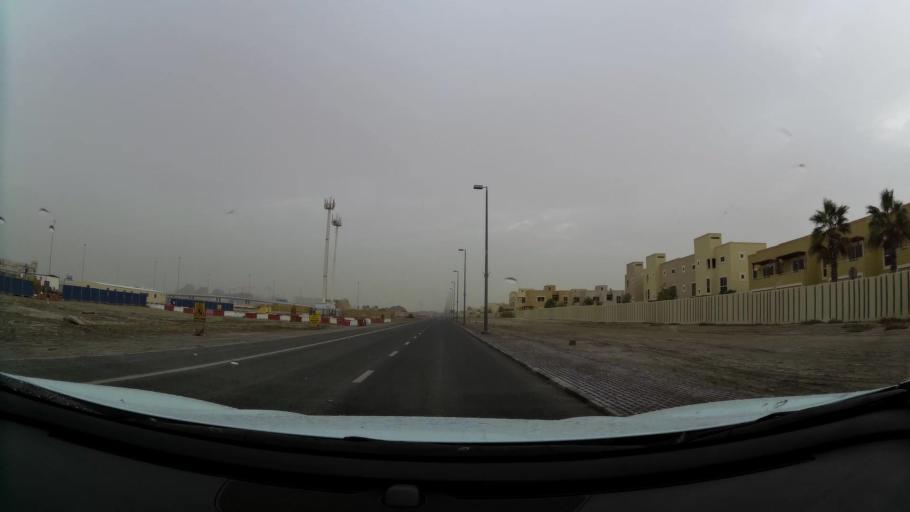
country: AE
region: Abu Dhabi
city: Abu Dhabi
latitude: 24.4396
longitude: 54.5889
